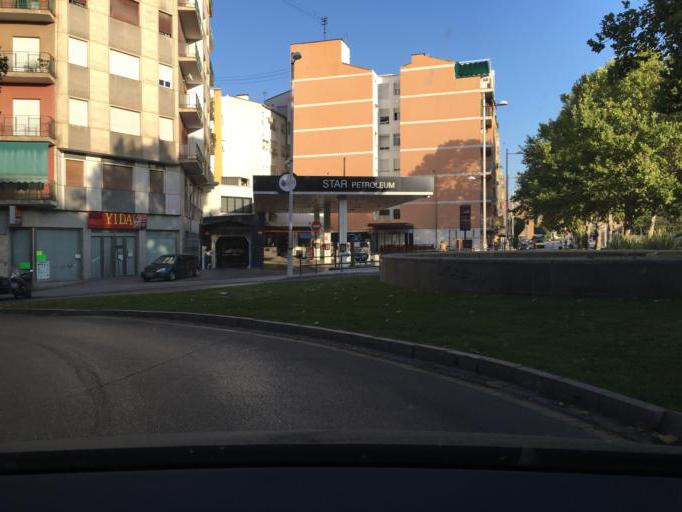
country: ES
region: Andalusia
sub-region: Provincia de Granada
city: Granada
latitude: 37.1897
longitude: -3.6059
